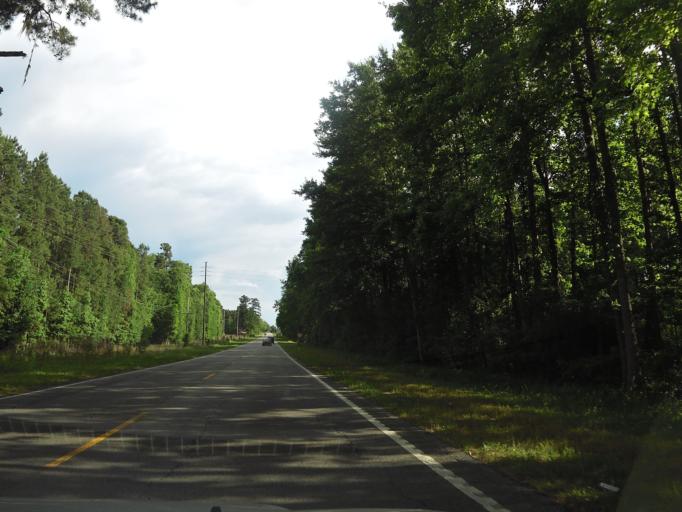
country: US
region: South Carolina
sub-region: Hampton County
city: Estill
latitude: 32.7717
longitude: -81.2410
